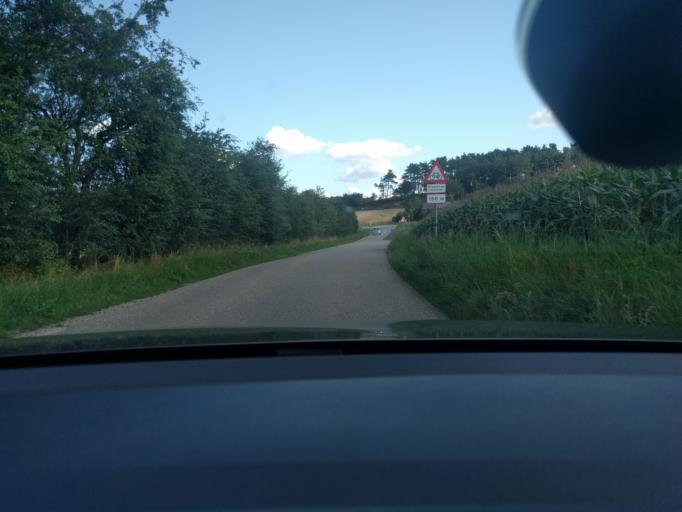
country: DK
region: Central Jutland
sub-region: Viborg Kommune
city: Viborg
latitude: 56.5248
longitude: 9.3251
